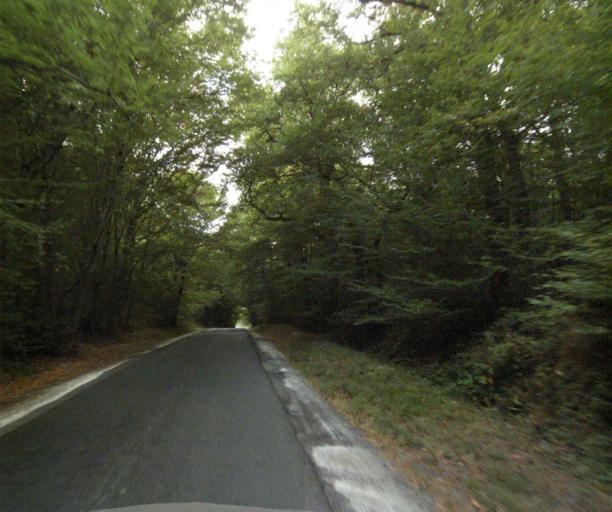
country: FR
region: Aquitaine
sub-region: Departement de la Gironde
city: La Sauve
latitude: 44.7864
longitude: -0.3240
